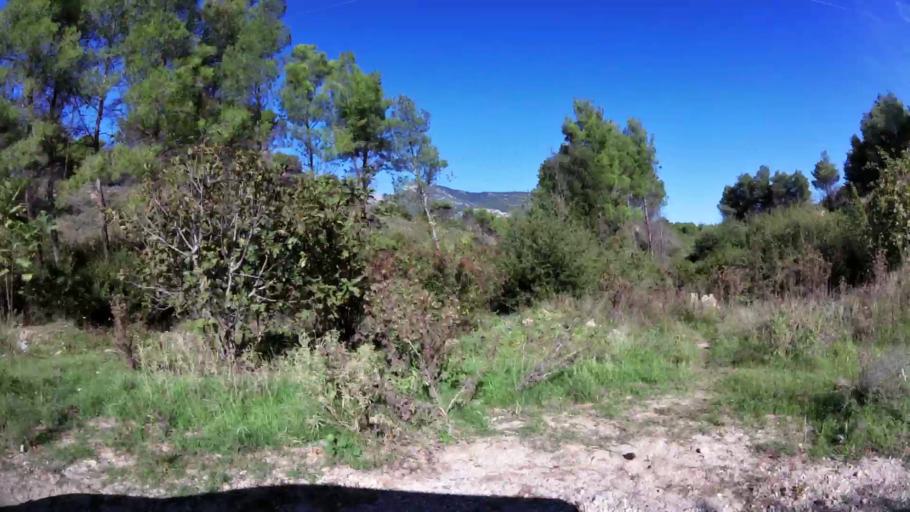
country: GR
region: Attica
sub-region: Nomarchia Anatolikis Attikis
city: Varybobi
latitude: 38.1252
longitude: 23.7776
